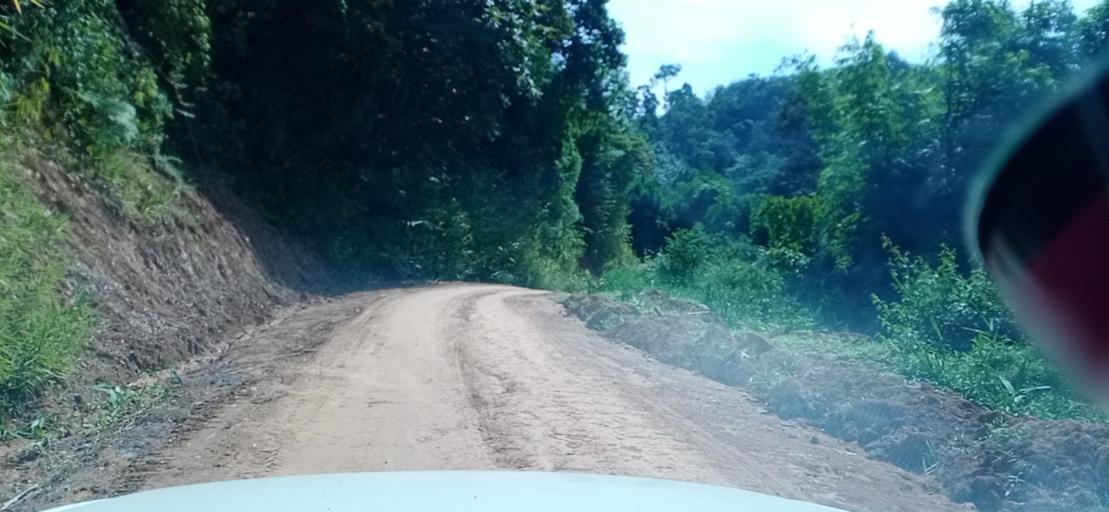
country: TH
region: Changwat Bueng Kan
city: Pak Khat
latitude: 18.6376
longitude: 103.2549
